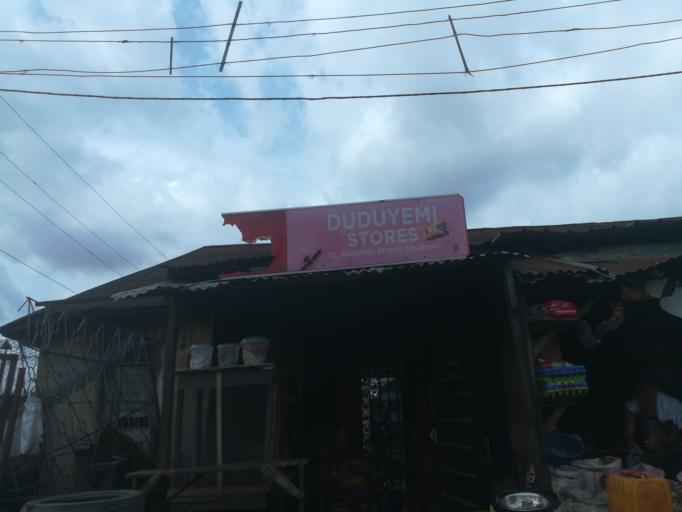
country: NG
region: Lagos
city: Somolu
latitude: 6.5312
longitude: 3.3831
